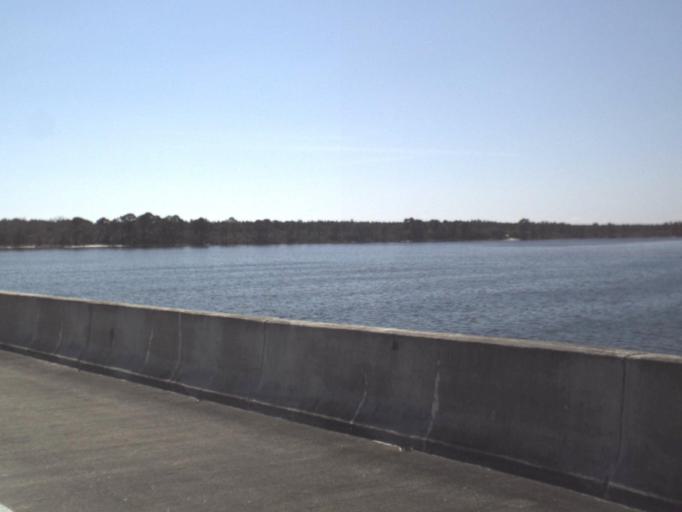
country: US
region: Florida
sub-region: Wakulla County
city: Crawfordville
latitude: 29.9658
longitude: -84.3842
